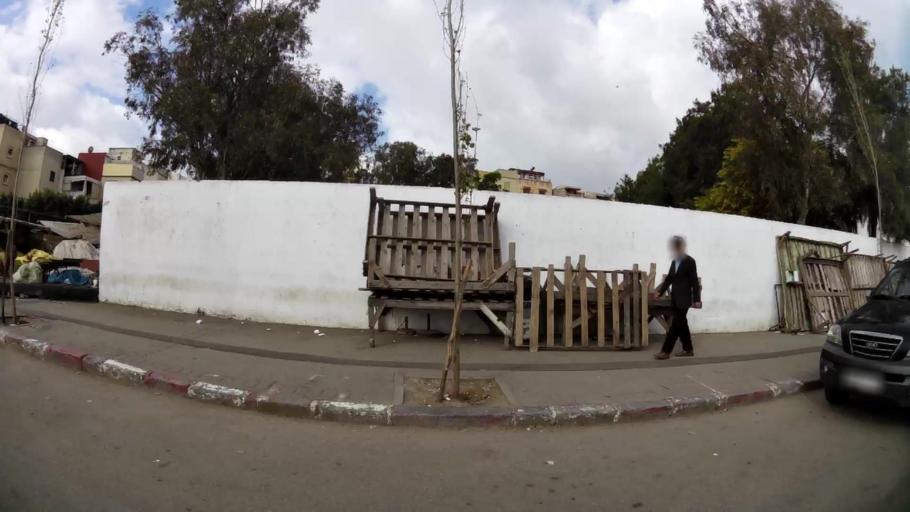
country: MA
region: Tanger-Tetouan
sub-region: Tanger-Assilah
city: Tangier
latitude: 35.7649
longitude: -5.8236
